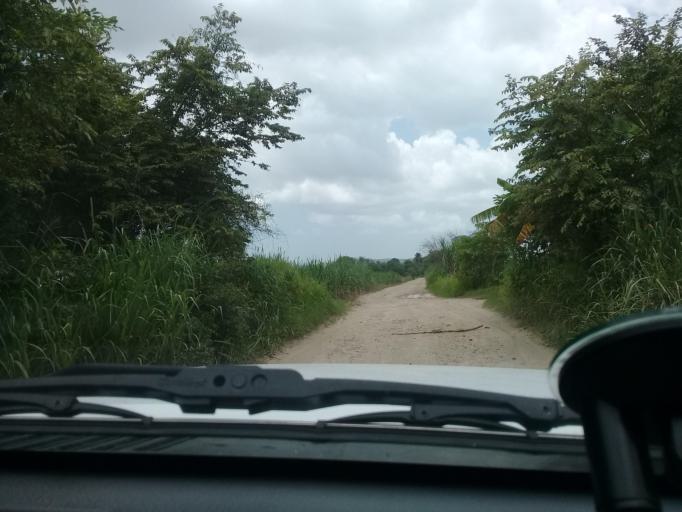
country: MX
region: Veracruz
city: Panuco
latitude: 22.1298
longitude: -98.0632
